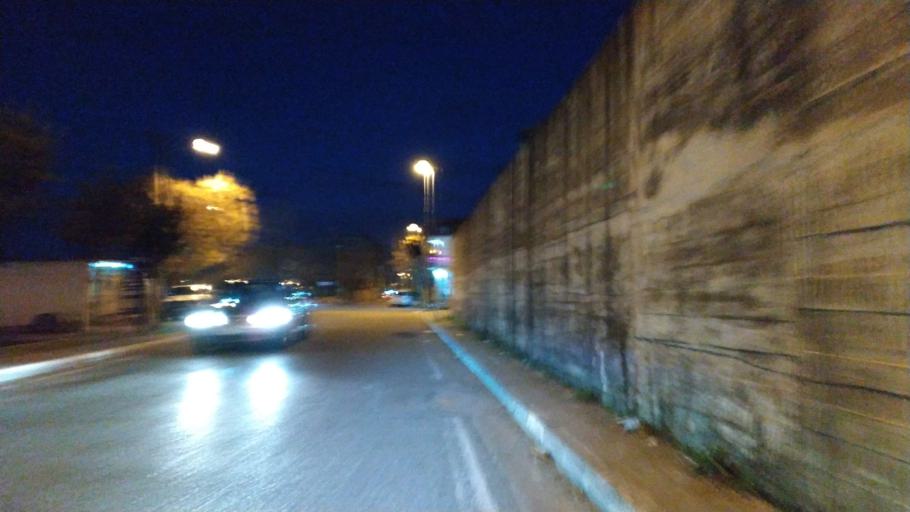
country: AL
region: Shkoder
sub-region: Rrethi i Shkodres
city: Shkoder
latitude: 42.0577
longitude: 19.5005
